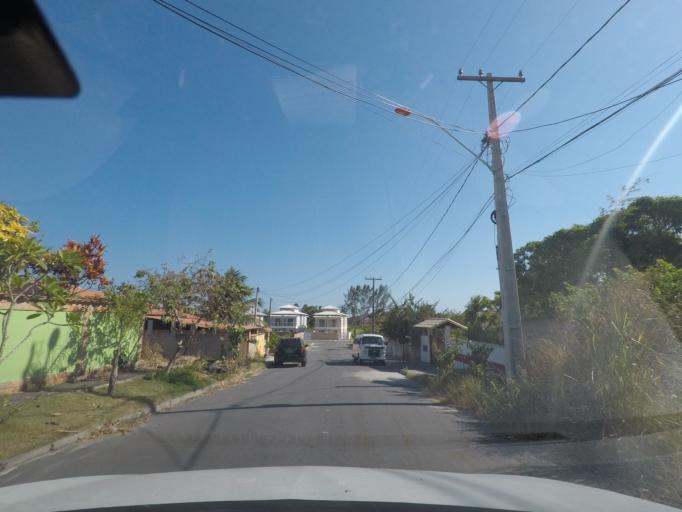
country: BR
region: Rio de Janeiro
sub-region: Marica
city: Marica
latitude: -22.9710
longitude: -42.9226
